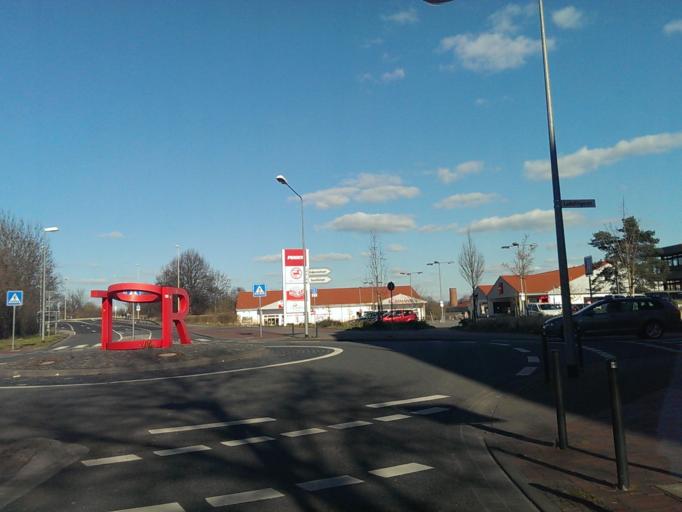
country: DE
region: Lower Saxony
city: Hildesheim
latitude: 52.1638
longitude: 9.9569
